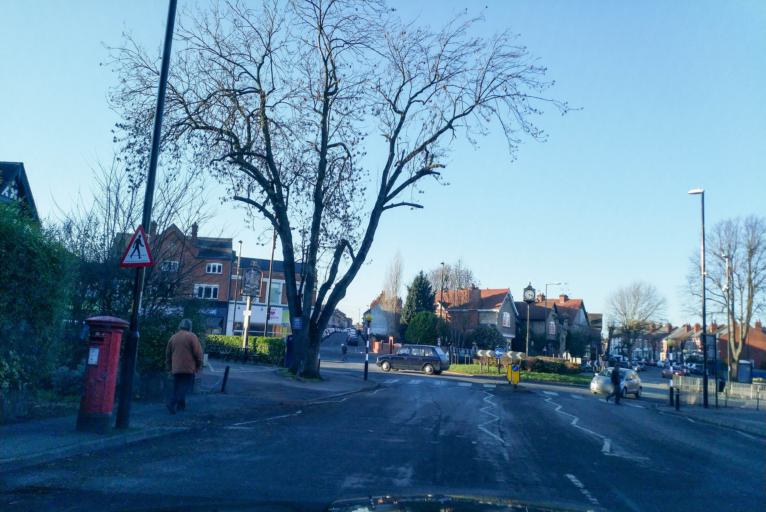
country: GB
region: England
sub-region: Coventry
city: Coventry
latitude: 52.3996
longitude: -1.5301
